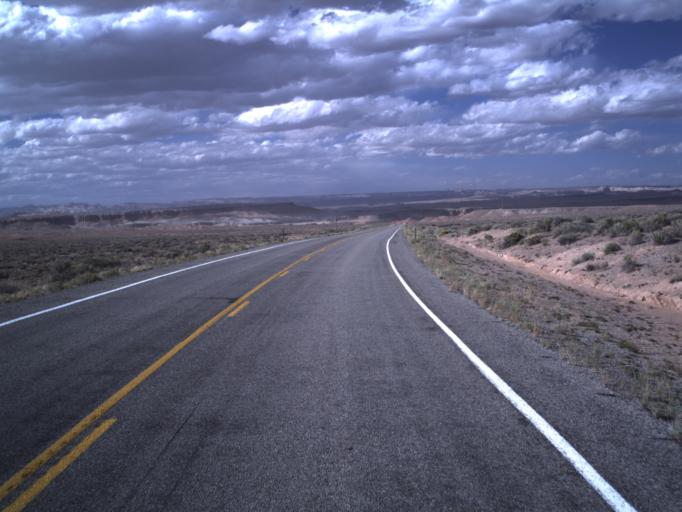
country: US
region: Utah
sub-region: Emery County
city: Ferron
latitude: 38.3407
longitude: -110.6907
